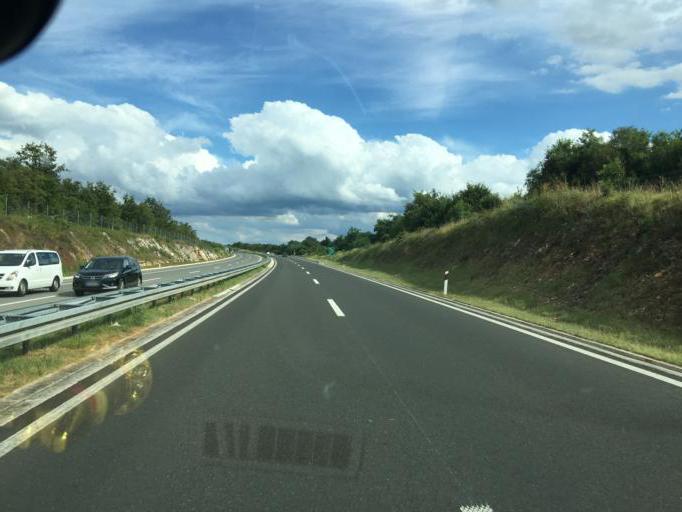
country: HR
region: Istarska
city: Vodnjan
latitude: 45.0959
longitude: 13.8225
